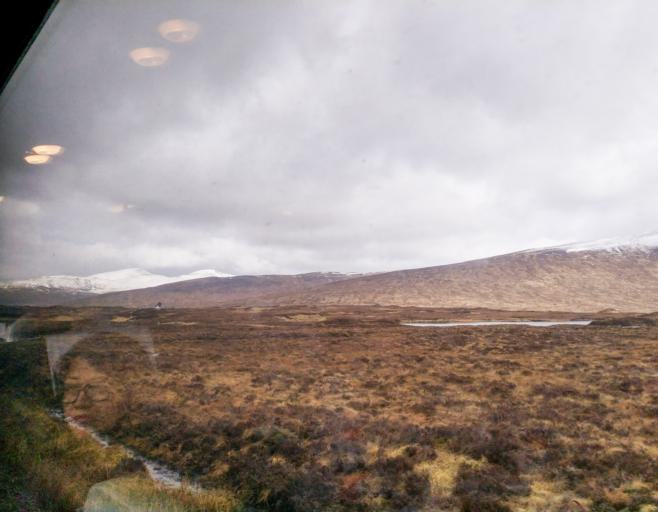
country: GB
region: Scotland
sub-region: Highland
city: Spean Bridge
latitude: 56.7525
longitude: -4.6798
